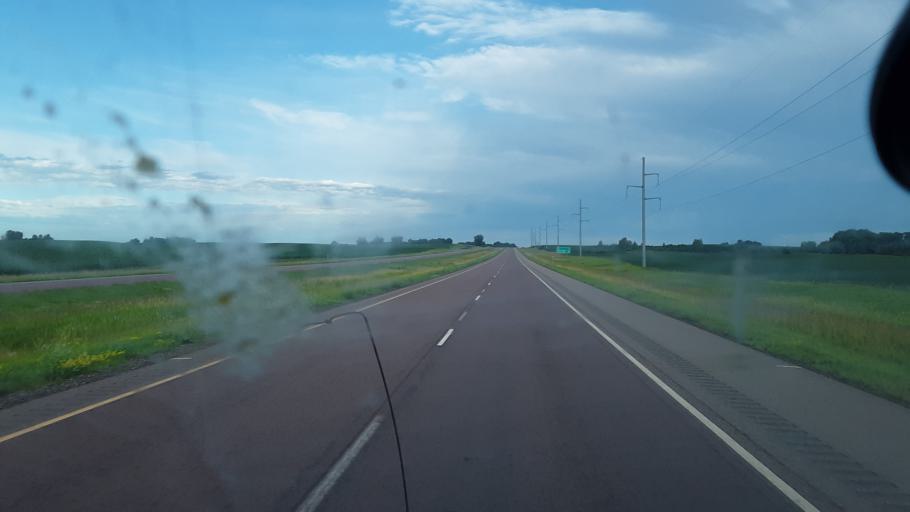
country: US
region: Minnesota
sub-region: Jackson County
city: Jackson
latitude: 43.6384
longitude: -95.0366
